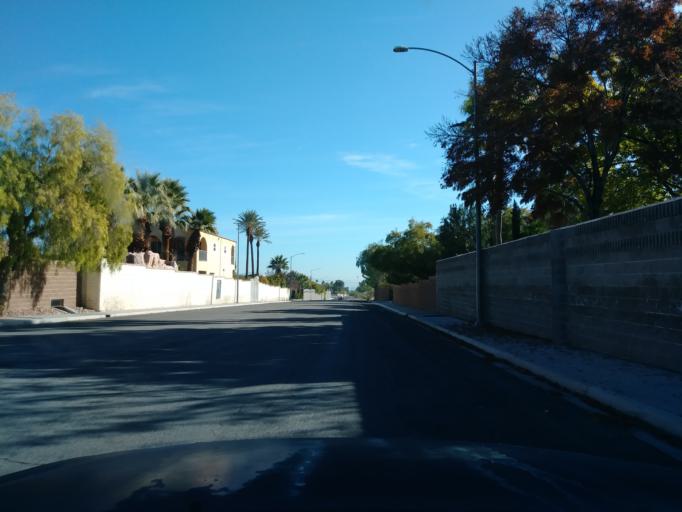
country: US
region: Nevada
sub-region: Clark County
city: Spring Valley
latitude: 36.1496
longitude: -115.2742
